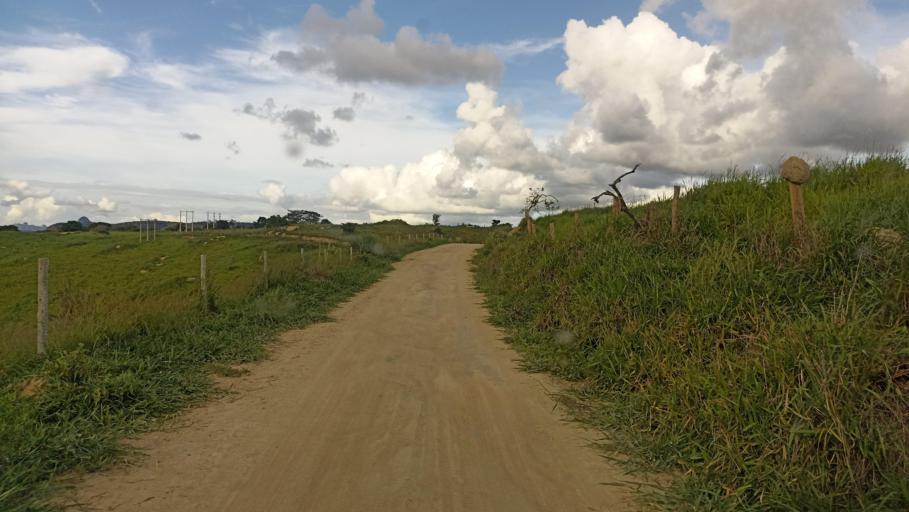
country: BR
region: Minas Gerais
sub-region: Almenara
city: Almenara
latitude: -16.5468
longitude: -40.4502
